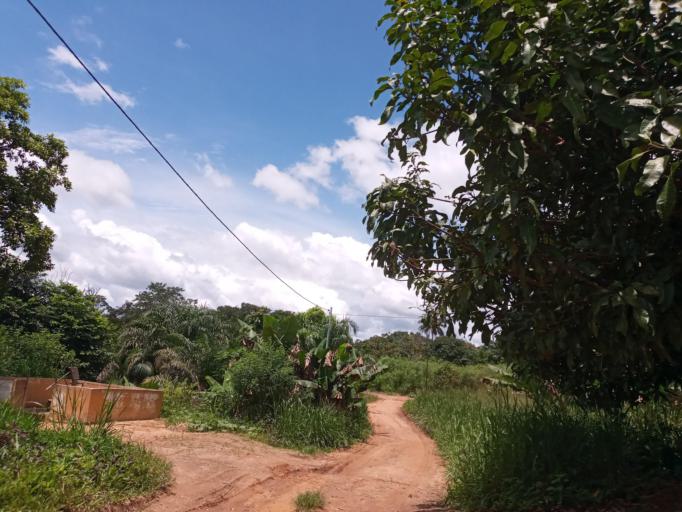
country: SL
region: Eastern Province
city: Tombu
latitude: 8.6283
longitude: -10.8232
